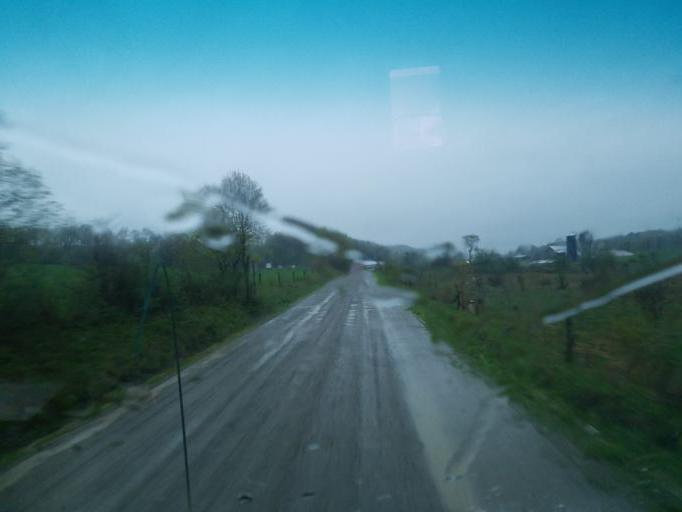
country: US
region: Pennsylvania
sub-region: Tioga County
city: Westfield
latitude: 41.9202
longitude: -77.7401
